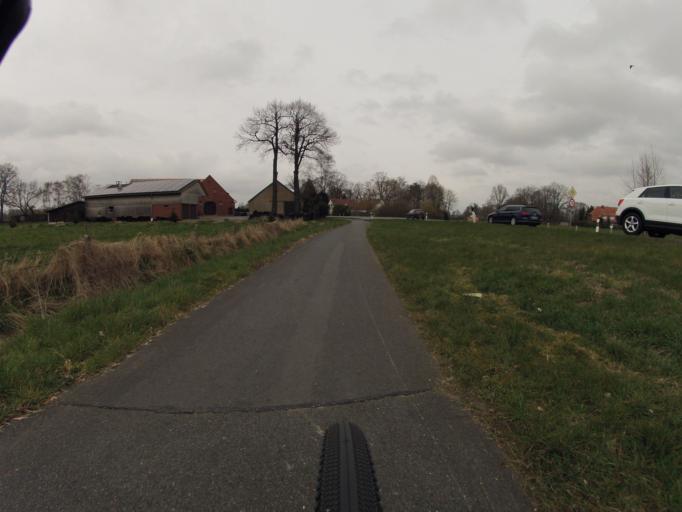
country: DE
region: North Rhine-Westphalia
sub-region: Regierungsbezirk Munster
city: Recke
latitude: 52.3515
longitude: 7.7271
